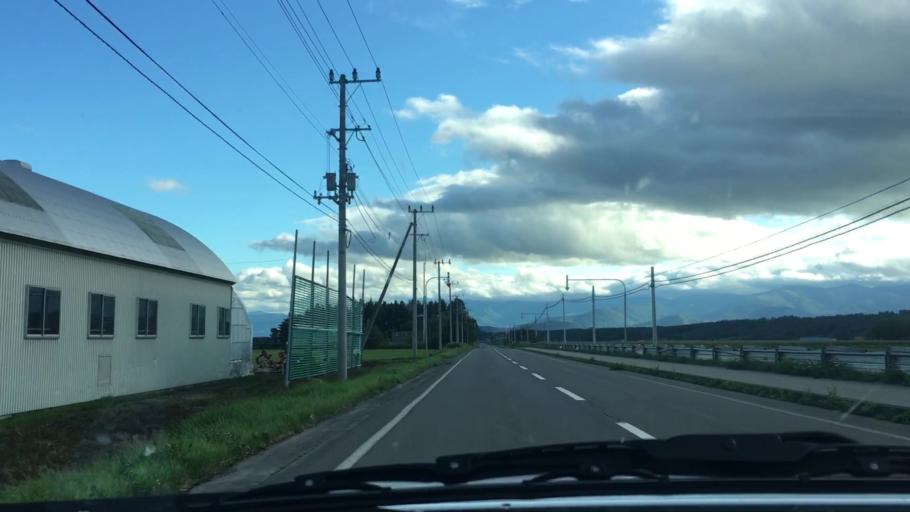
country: JP
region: Hokkaido
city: Otofuke
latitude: 43.1468
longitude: 142.8984
